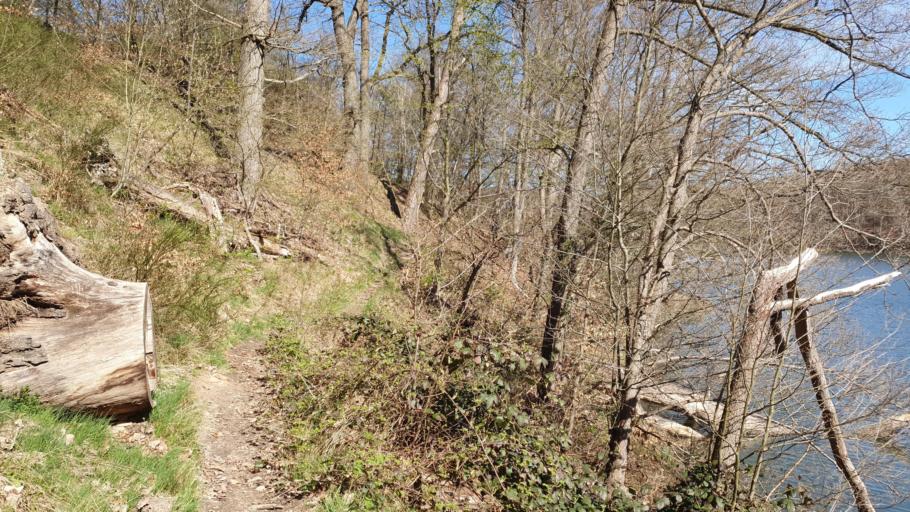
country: DE
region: Mecklenburg-Vorpommern
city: Bruel
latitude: 53.7137
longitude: 11.6967
